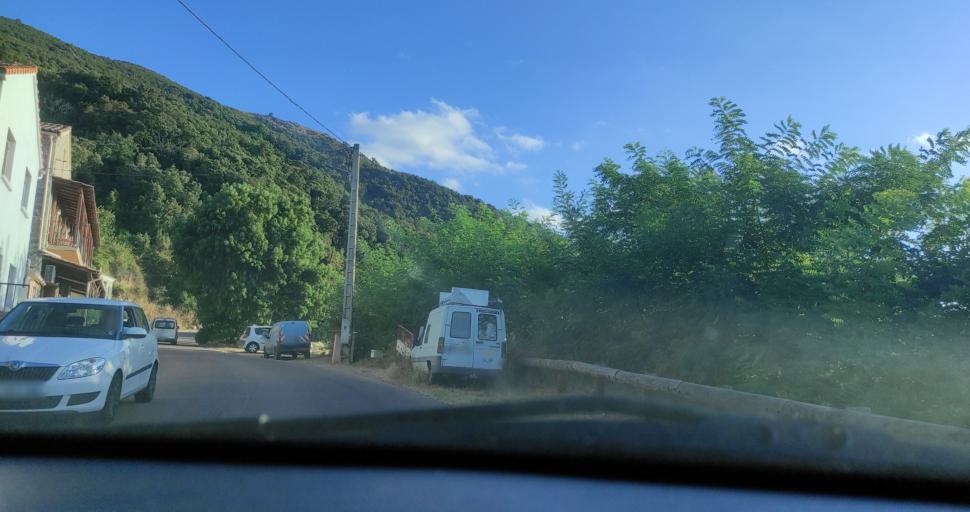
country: FR
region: Corsica
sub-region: Departement de la Corse-du-Sud
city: Appietto
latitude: 42.0282
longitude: 8.7518
